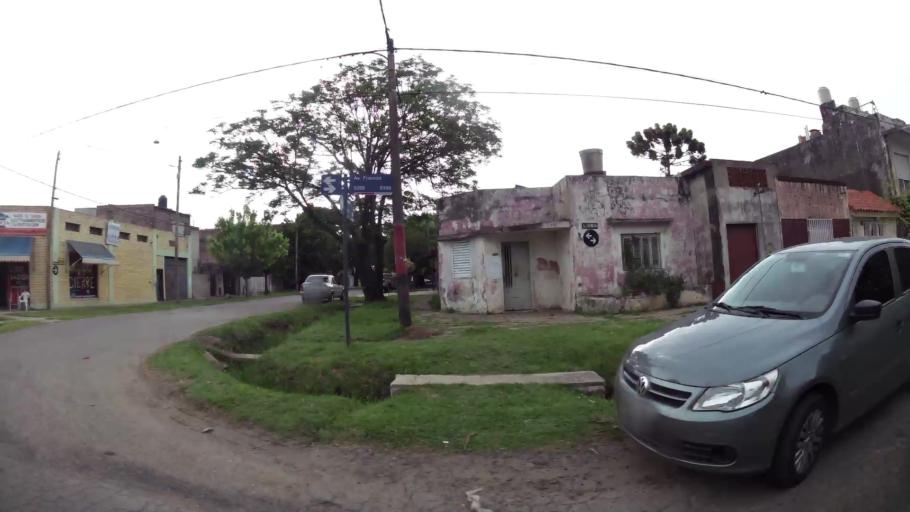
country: AR
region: Santa Fe
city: Gobernador Galvez
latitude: -32.9987
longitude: -60.6779
